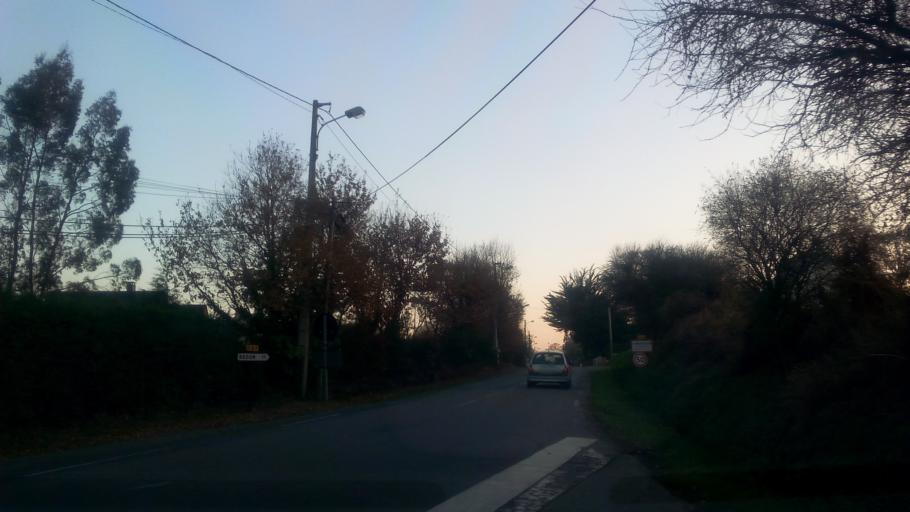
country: FR
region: Brittany
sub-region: Departement d'Ille-et-Vilaine
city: Bains-sur-Oust
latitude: 47.7382
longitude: -2.0498
